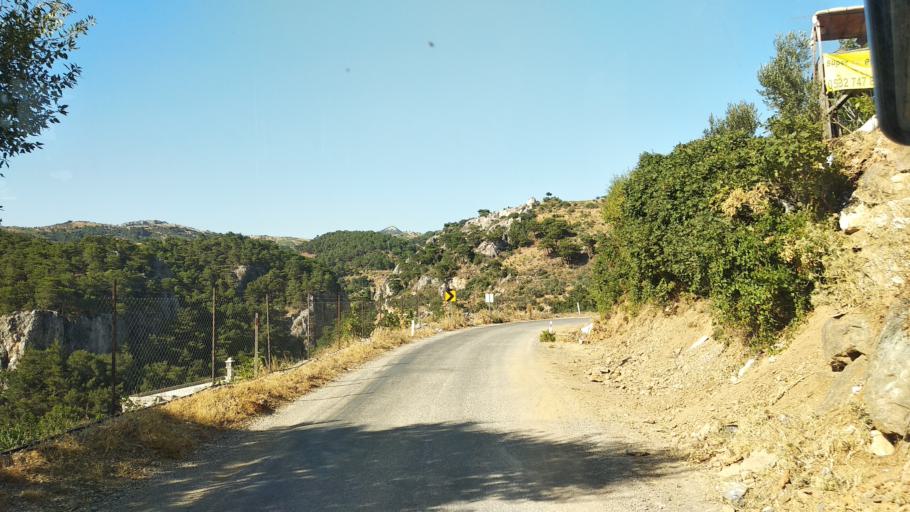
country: TR
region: Izmir
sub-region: Seferihisar
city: Seferhisar
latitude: 38.3151
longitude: 26.9554
